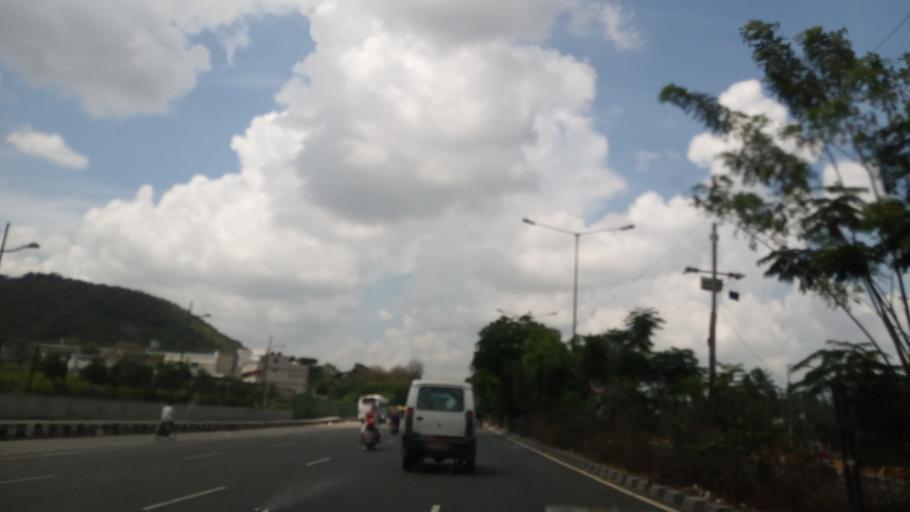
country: IN
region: Tamil Nadu
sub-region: Kancheepuram
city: Vandalur
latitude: 12.8990
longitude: 80.0907
